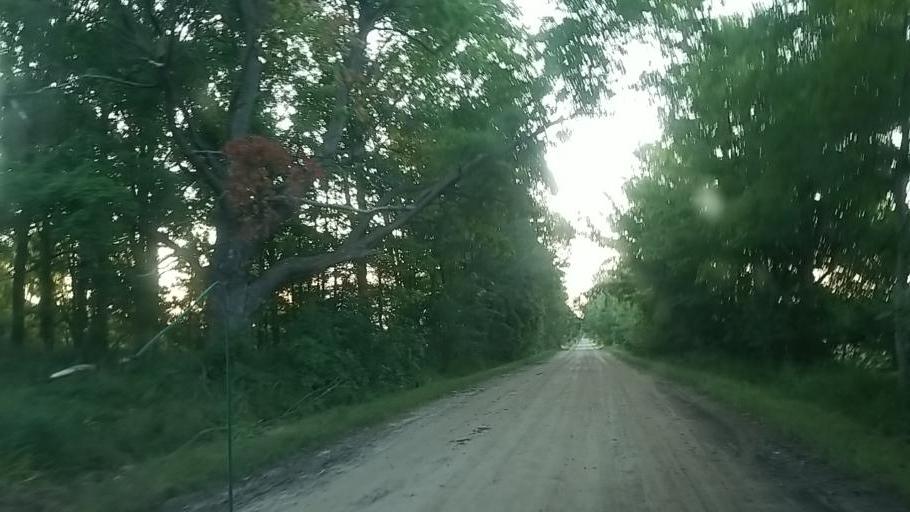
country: US
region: Michigan
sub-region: Osceola County
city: Evart
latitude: 43.9151
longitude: -85.1877
